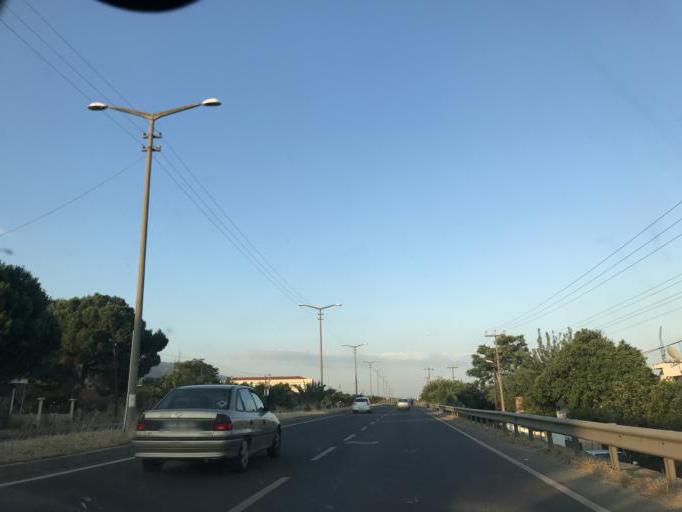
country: TR
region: Aydin
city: Kuyucak
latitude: 37.9088
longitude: 28.4592
